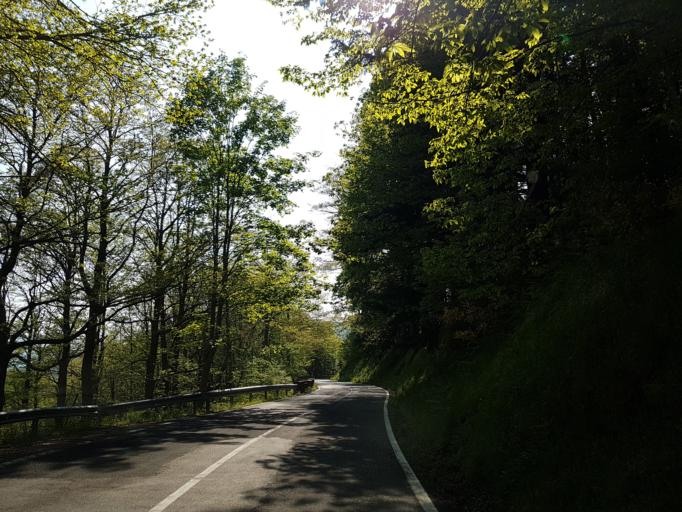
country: IT
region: Emilia-Romagna
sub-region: Forli-Cesena
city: San Piero in Bagno
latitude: 43.7939
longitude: 11.8949
